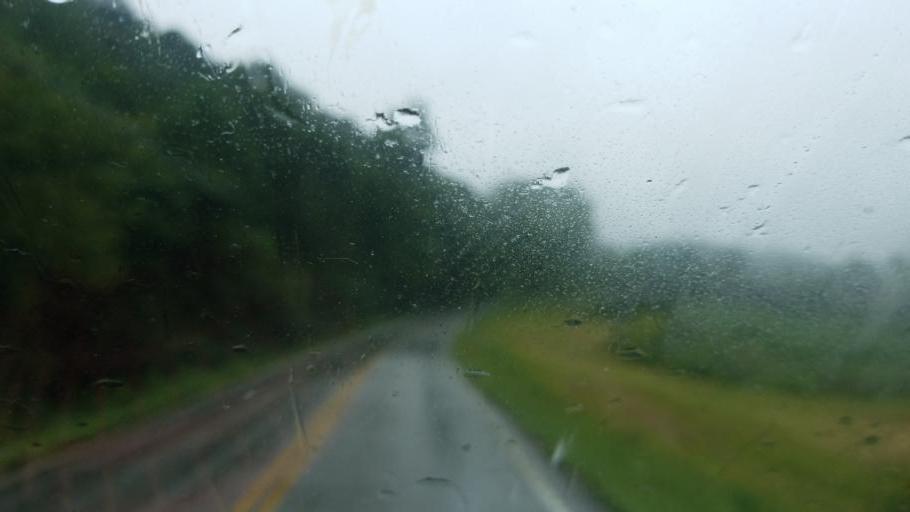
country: US
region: Kentucky
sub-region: Greenup County
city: South Shore
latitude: 38.6894
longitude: -82.9360
